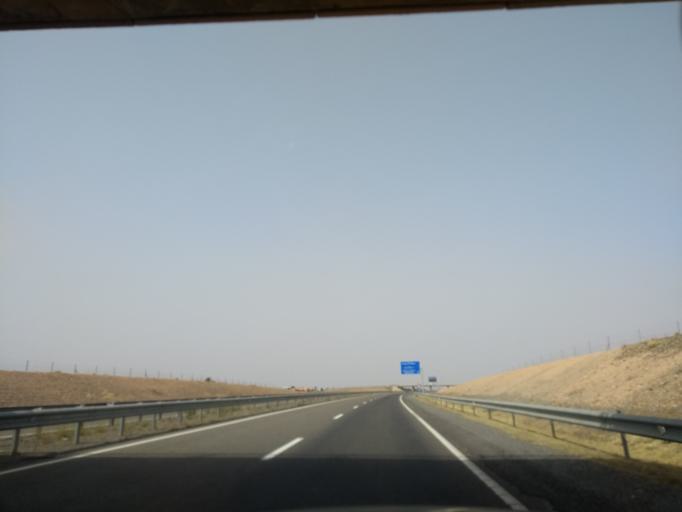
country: MA
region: Marrakech-Tensift-Al Haouz
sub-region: Marrakech
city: Marrakesh
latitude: 31.7230
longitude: -8.2268
